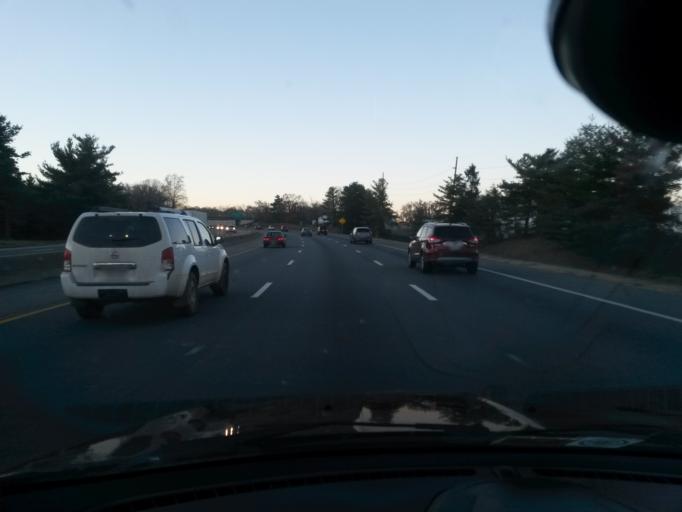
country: US
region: Virginia
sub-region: City of Roanoke
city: Roanoke
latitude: 37.2879
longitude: -79.9392
